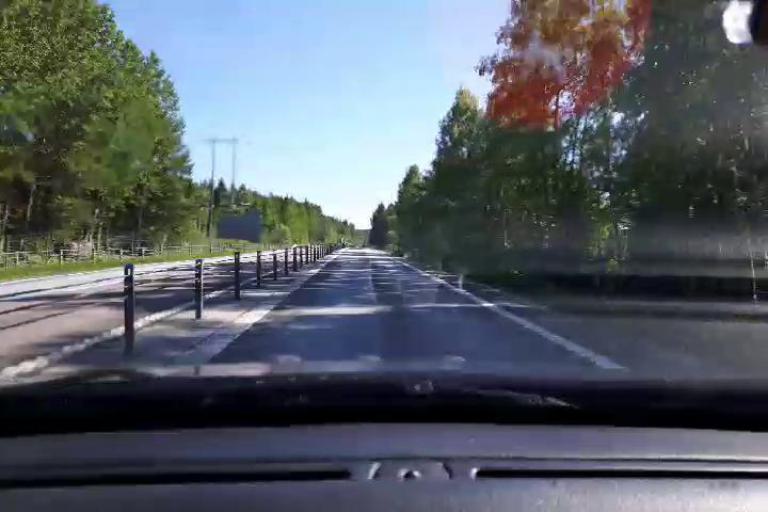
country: SE
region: Gaevleborg
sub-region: Soderhamns Kommun
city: Soderhamn
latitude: 61.2873
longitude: 17.0238
